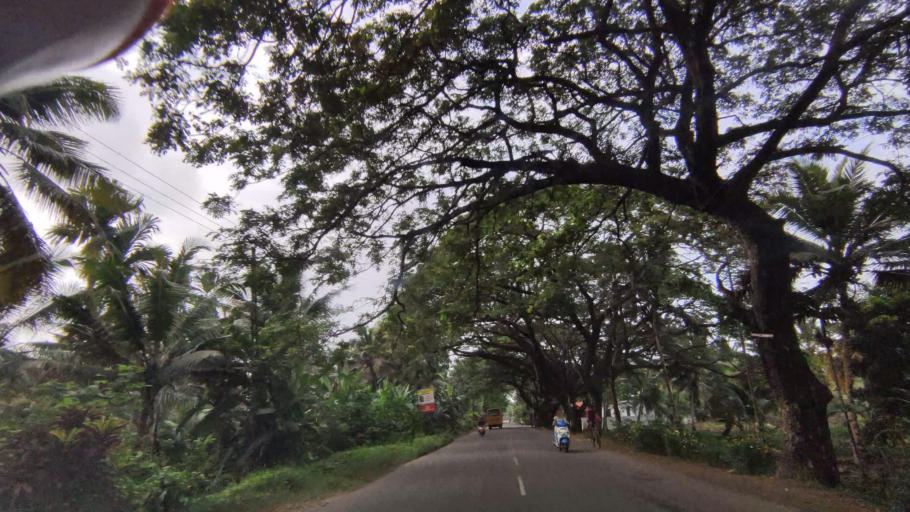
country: IN
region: Kerala
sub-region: Alappuzha
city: Shertallai
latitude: 9.6336
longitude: 76.4300
